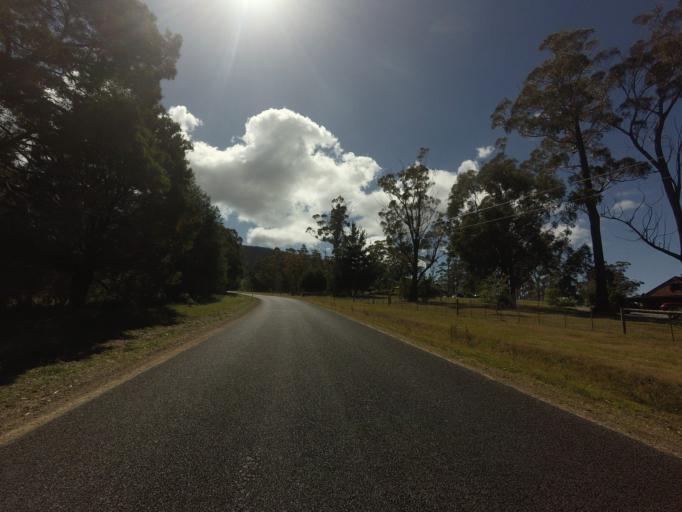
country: AU
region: Tasmania
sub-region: Break O'Day
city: St Helens
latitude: -41.6447
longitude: 148.2427
